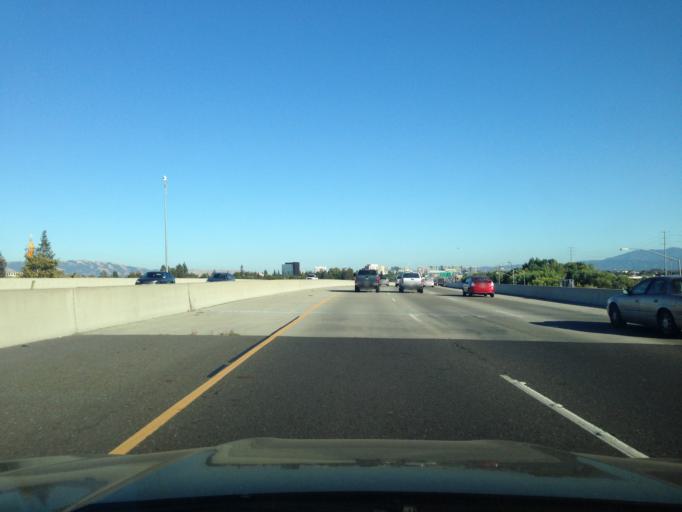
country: US
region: California
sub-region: Santa Clara County
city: San Jose
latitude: 37.3654
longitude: -121.9197
